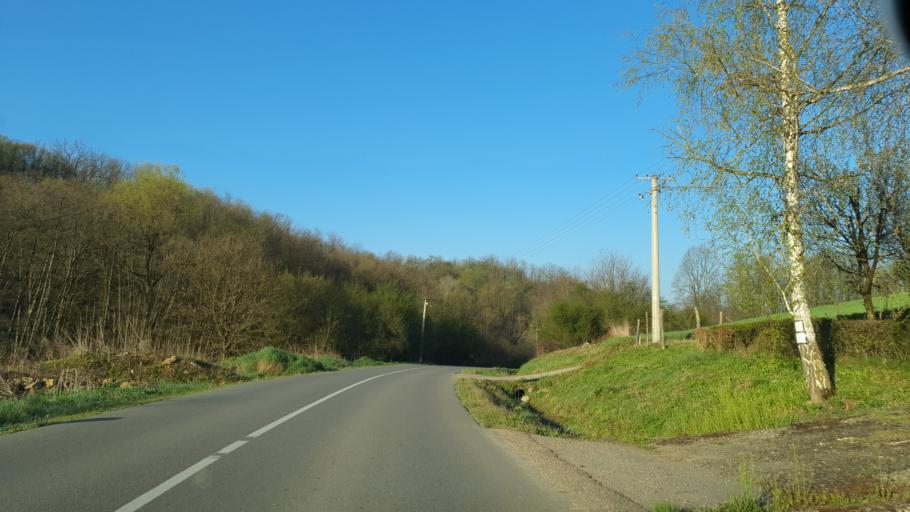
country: RS
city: Bukor
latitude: 44.4580
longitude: 19.4909
